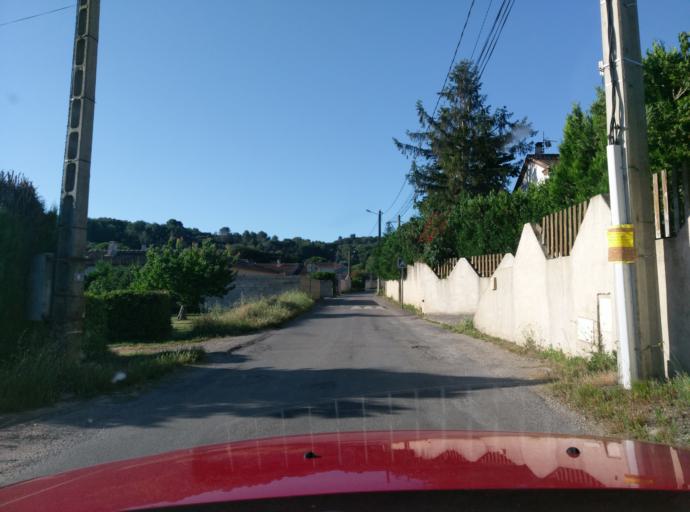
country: FR
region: Languedoc-Roussillon
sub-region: Departement du Gard
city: Comps
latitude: 43.8490
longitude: 4.5980
